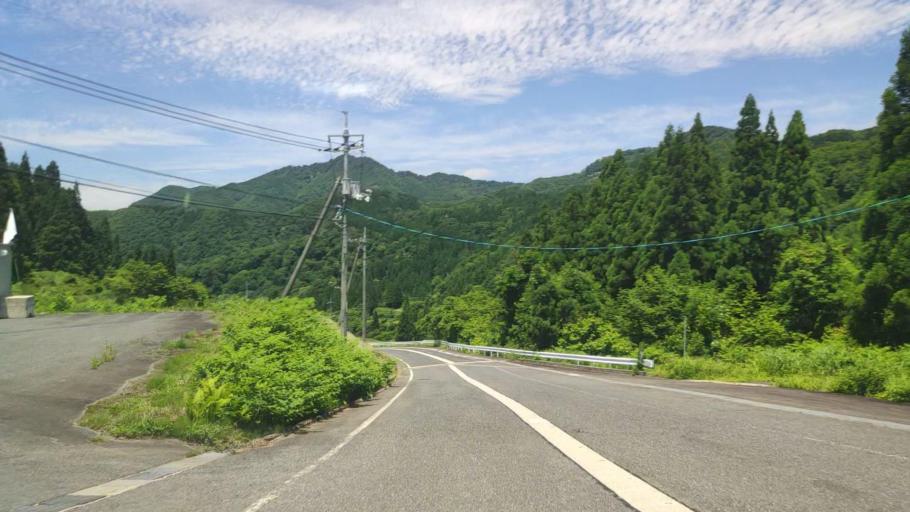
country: JP
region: Tottori
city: Tottori
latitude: 35.3547
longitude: 134.4862
